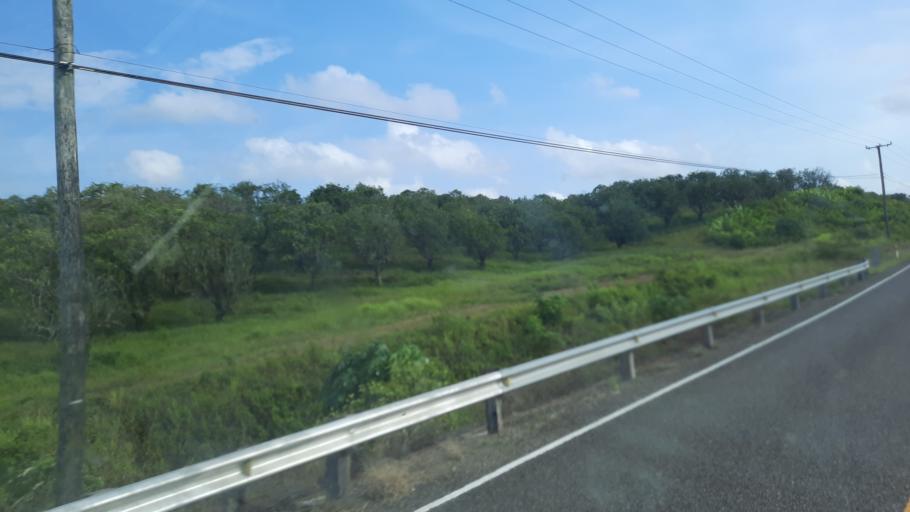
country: BZ
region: Cayo
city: Belmopan
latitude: 17.1142
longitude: -88.6571
